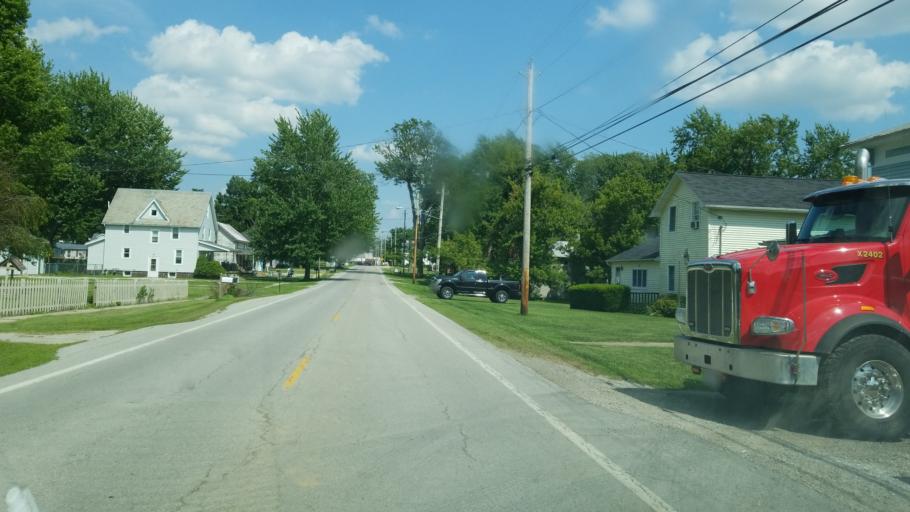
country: US
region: Ohio
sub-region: Huron County
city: Plymouth
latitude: 41.1041
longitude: -82.6170
